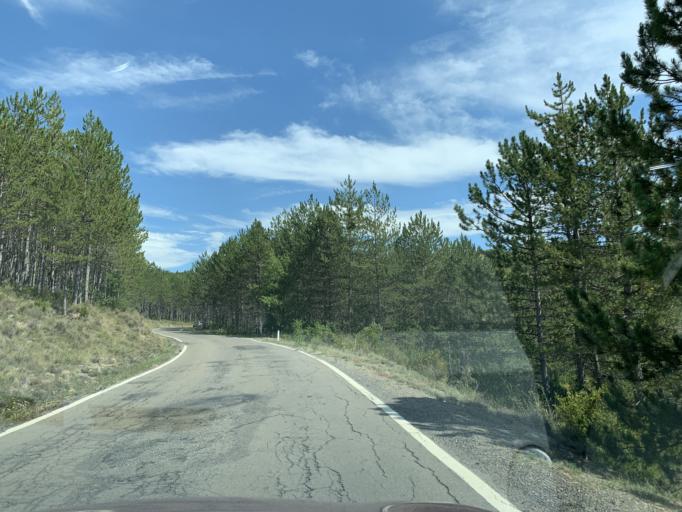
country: ES
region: Aragon
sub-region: Provincia de Huesca
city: Santa Cruz de la Seros
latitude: 42.6000
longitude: -0.6557
